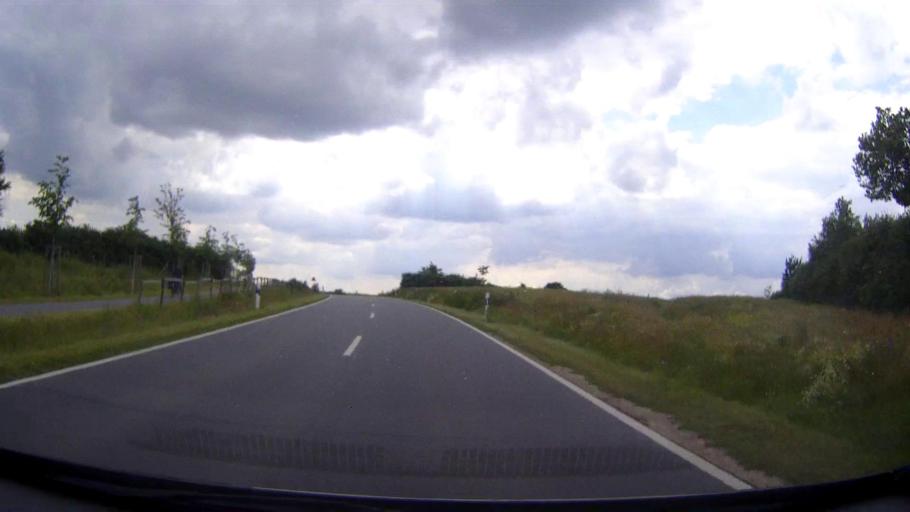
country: DE
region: Schleswig-Holstein
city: Stockelsdorf
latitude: 53.8886
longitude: 10.6096
